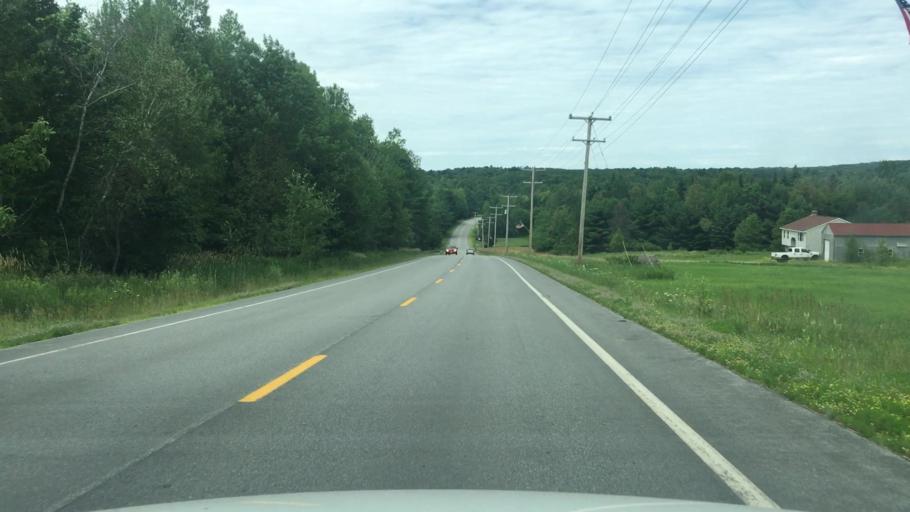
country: US
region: Maine
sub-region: Waldo County
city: Troy
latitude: 44.5342
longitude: -69.2795
